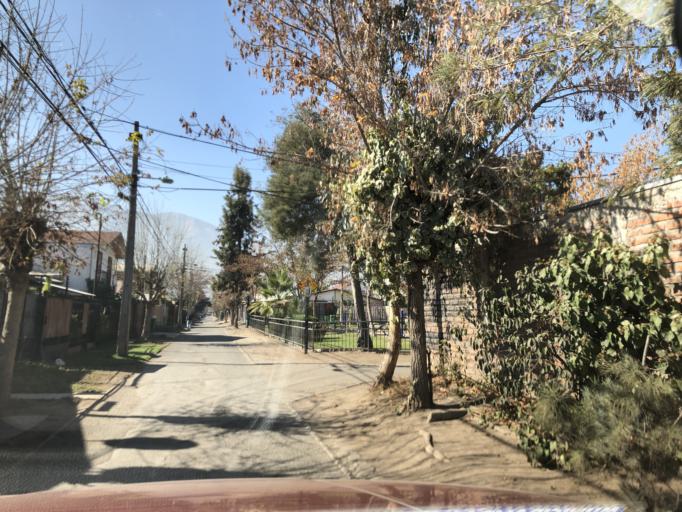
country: CL
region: Santiago Metropolitan
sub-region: Provincia de Cordillera
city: Puente Alto
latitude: -33.5689
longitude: -70.5757
